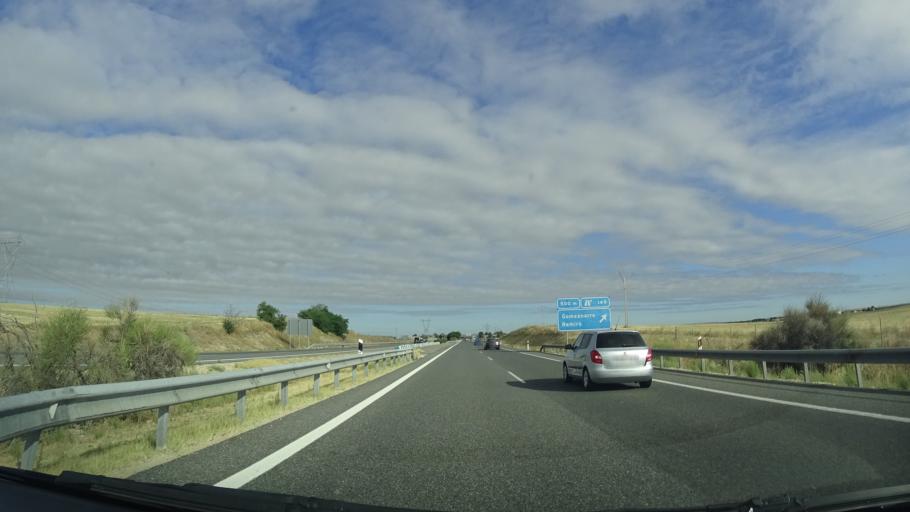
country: ES
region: Castille and Leon
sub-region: Provincia de Valladolid
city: San Vicente del Palacio
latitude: 41.2307
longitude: -4.8528
